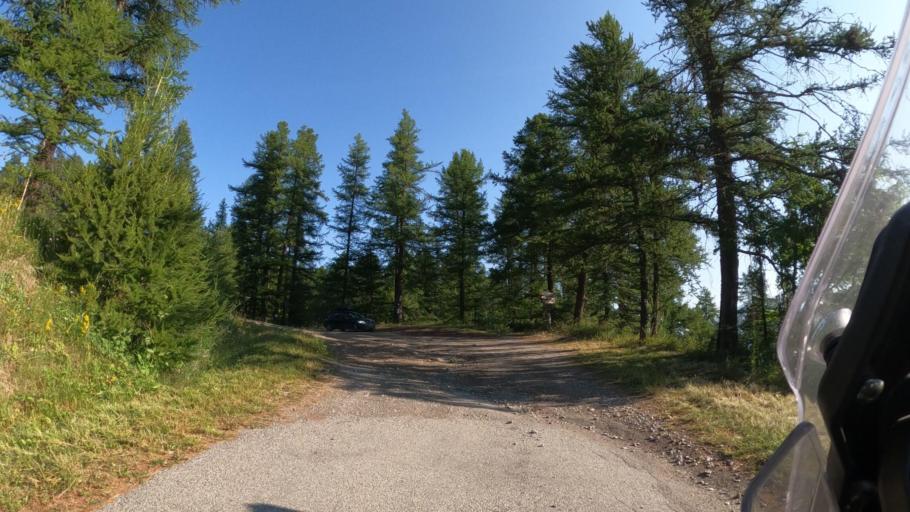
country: FR
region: Provence-Alpes-Cote d'Azur
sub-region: Departement des Hautes-Alpes
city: Guillestre
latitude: 44.6070
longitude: 6.6735
